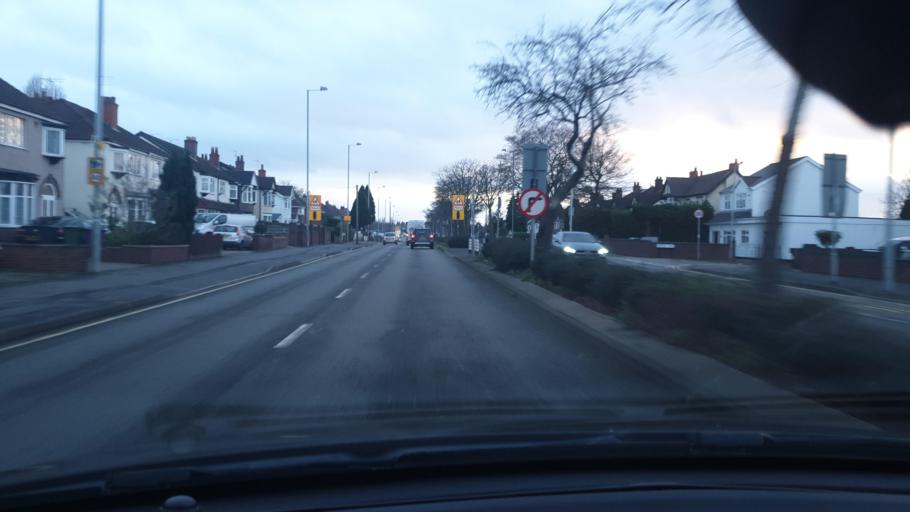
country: GB
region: England
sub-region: Wolverhampton
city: Wolverhampton
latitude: 52.6247
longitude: -2.1279
